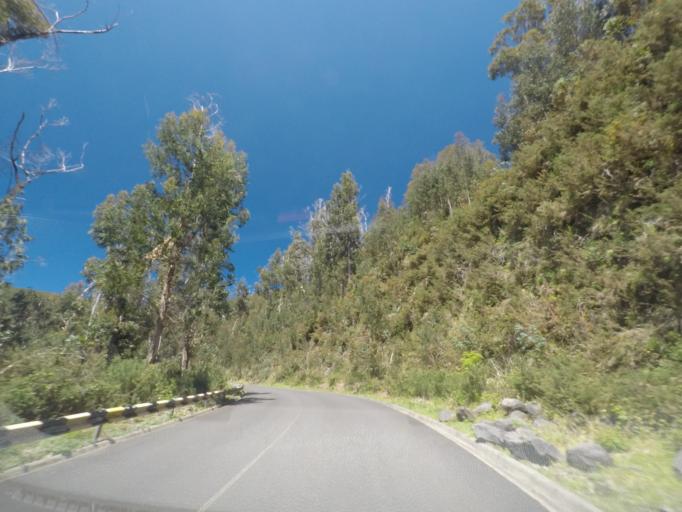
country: PT
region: Madeira
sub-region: Calheta
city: Arco da Calheta
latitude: 32.7413
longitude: -17.1274
